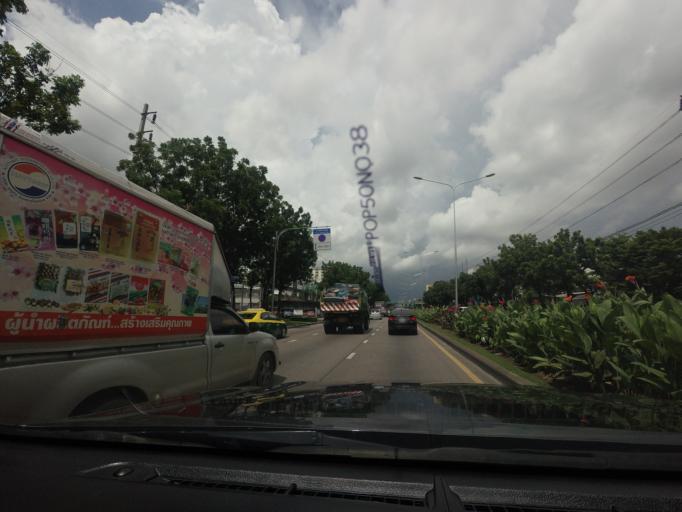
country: TH
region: Bangkok
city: Nong Khaem
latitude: 13.7075
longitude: 100.3708
